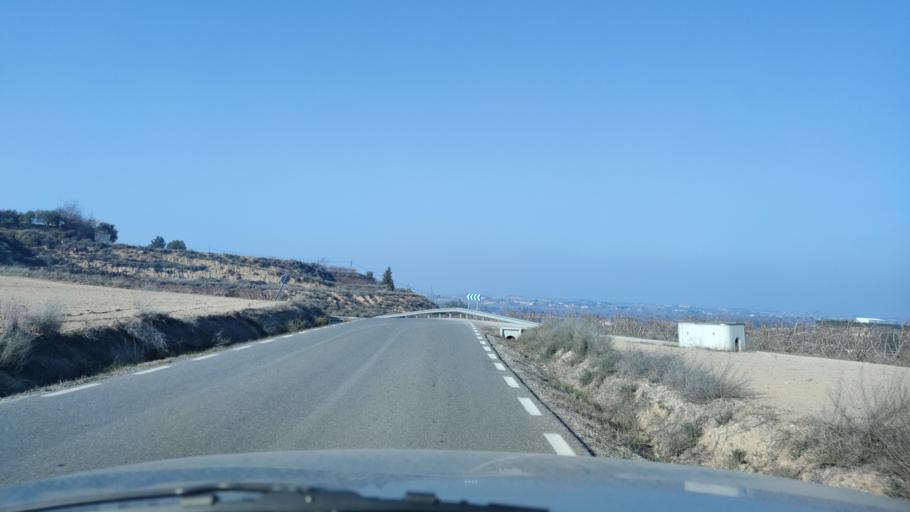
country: ES
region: Catalonia
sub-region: Provincia de Lleida
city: Sunyer
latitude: 41.5545
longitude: 0.5731
